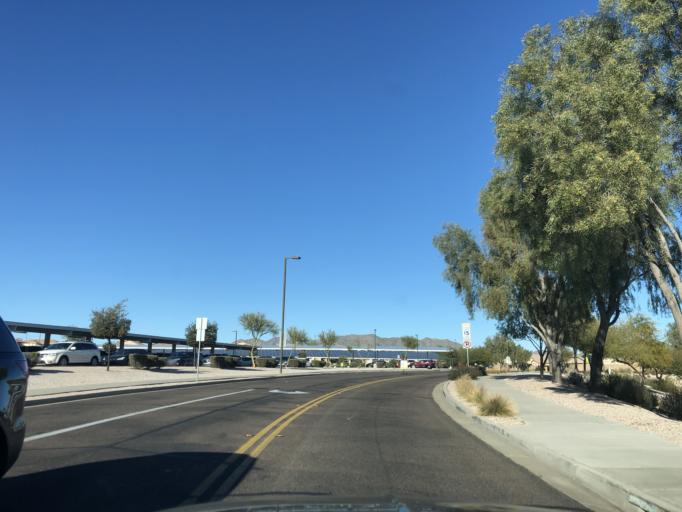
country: US
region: Arizona
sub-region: Maricopa County
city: Buckeye
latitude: 33.4212
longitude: -112.6053
